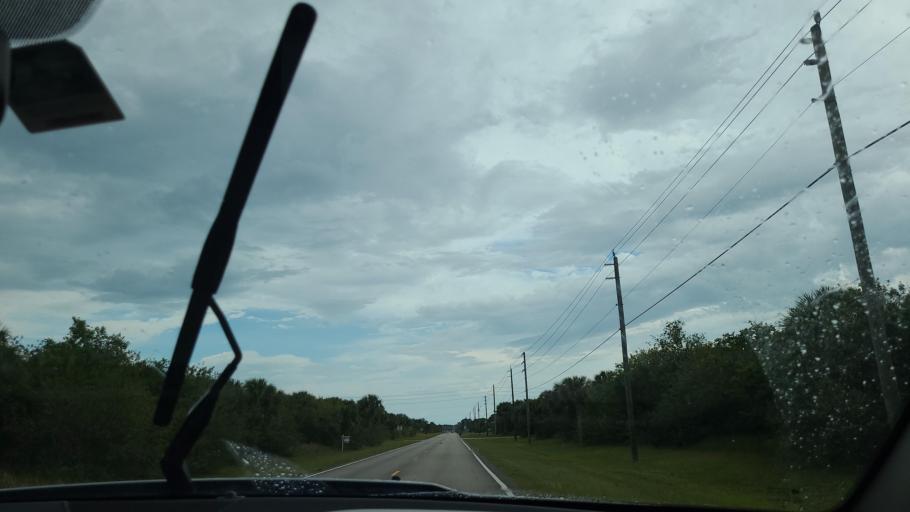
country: US
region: Florida
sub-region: Brevard County
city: June Park
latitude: 27.9528
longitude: -80.6939
